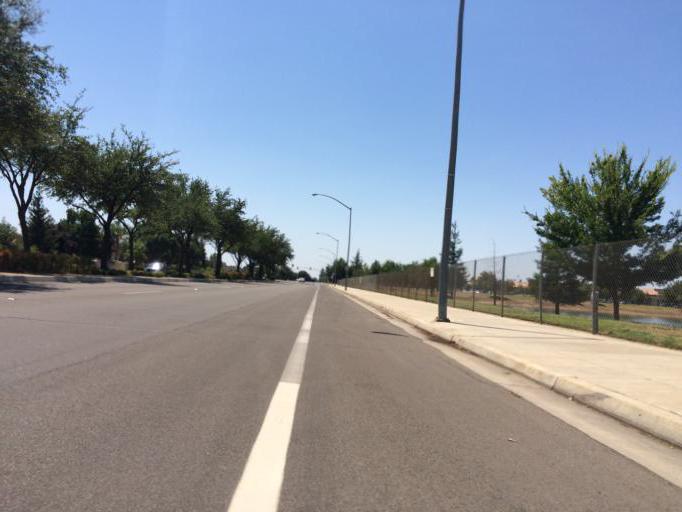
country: US
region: California
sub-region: Fresno County
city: Clovis
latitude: 36.8690
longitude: -119.7390
